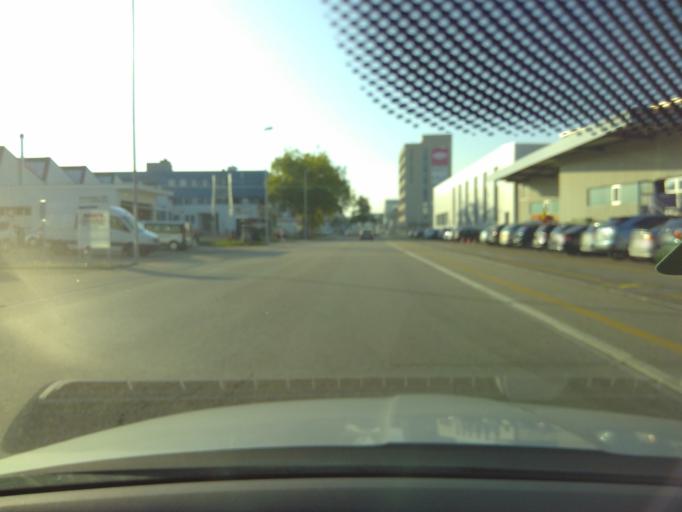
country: CH
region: Zurich
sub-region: Bezirk Dielsdorf
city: Regensdorf / Feldblumen-Riedthofstrasse
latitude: 47.4434
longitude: 8.4636
